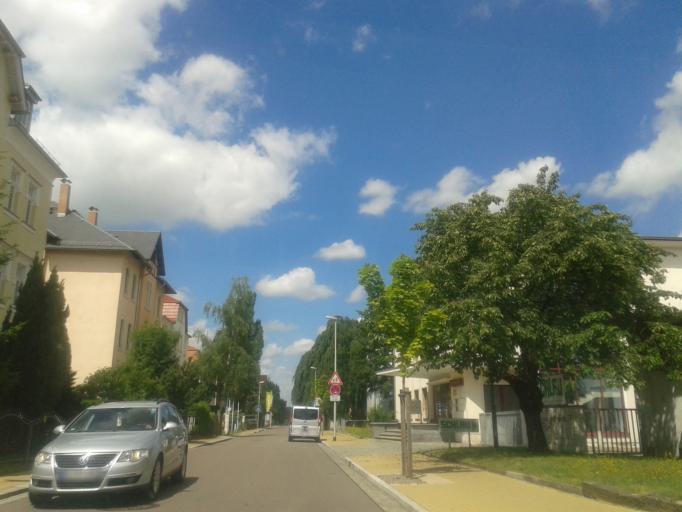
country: DE
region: Saxony
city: Radebeul
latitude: 51.0952
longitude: 13.6850
